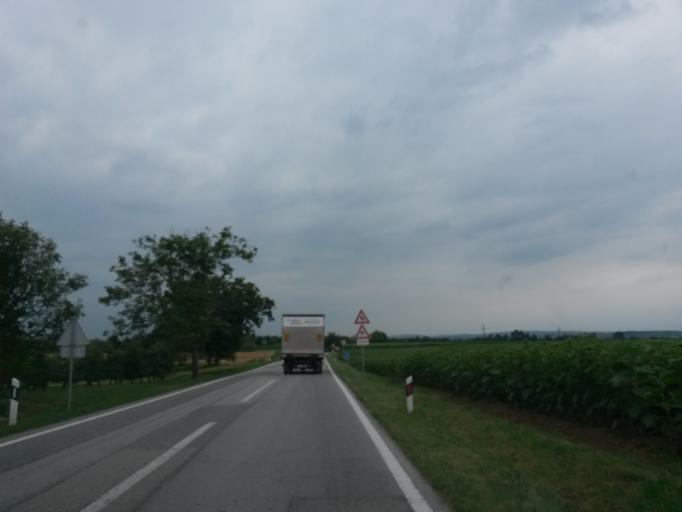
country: HR
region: Vukovarsko-Srijemska
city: Ilok
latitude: 45.2281
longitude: 19.3297
